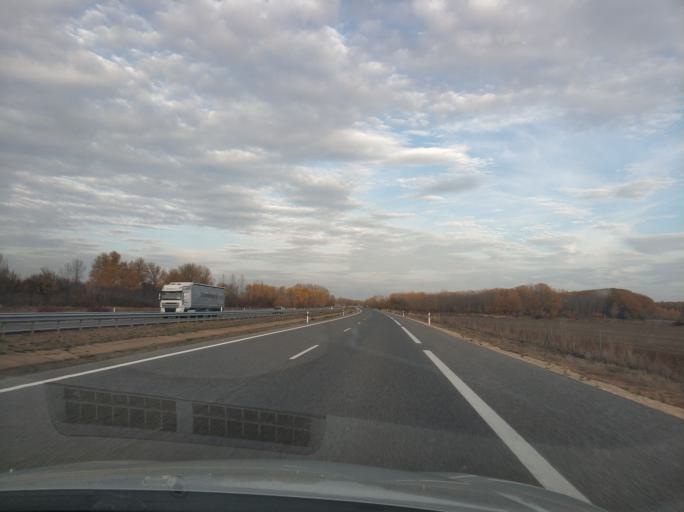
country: ES
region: Castille and Leon
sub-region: Provincia de Palencia
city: Osornillo
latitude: 42.4043
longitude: -4.3035
